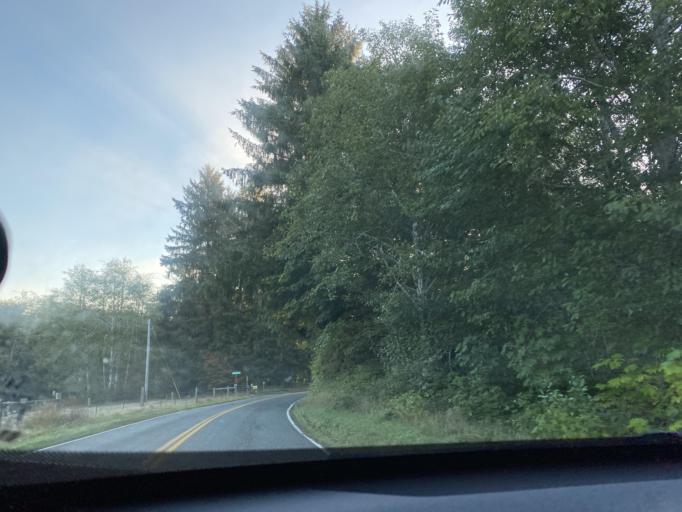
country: US
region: Washington
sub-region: Clallam County
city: Forks
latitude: 47.8167
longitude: -124.1628
